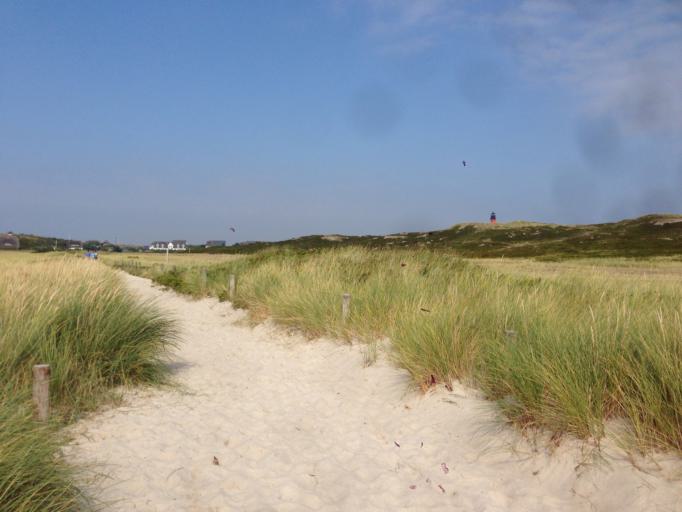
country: DE
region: Schleswig-Holstein
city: Norddorf
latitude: 54.7487
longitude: 8.2875
